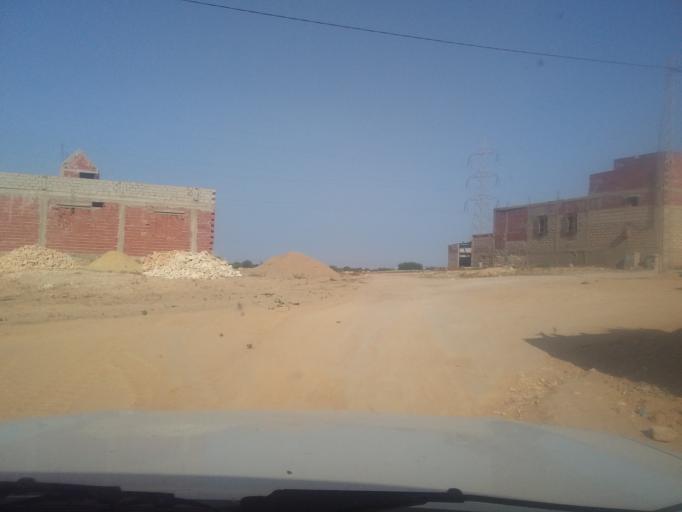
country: TN
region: Qabis
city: Matmata
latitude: 33.5849
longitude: 10.2691
